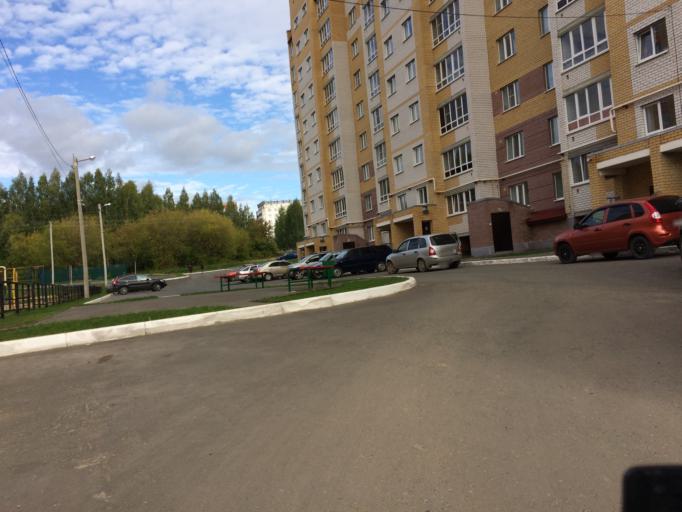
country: RU
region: Mariy-El
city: Yoshkar-Ola
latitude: 56.6509
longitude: 47.9669
